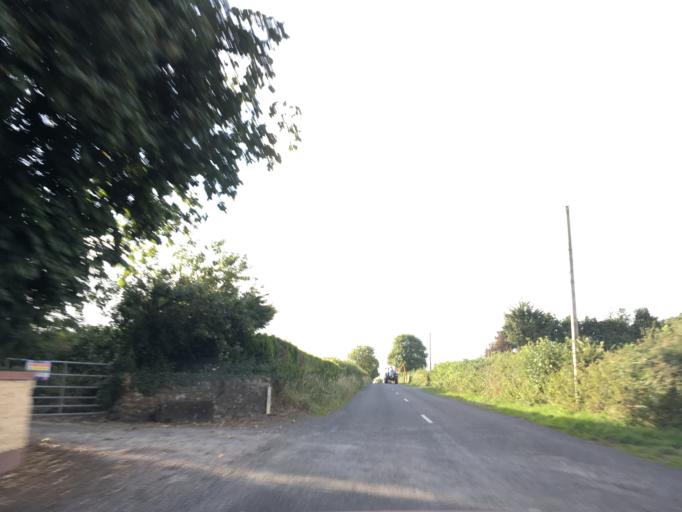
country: IE
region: Munster
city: Cashel
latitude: 52.4719
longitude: -7.9231
